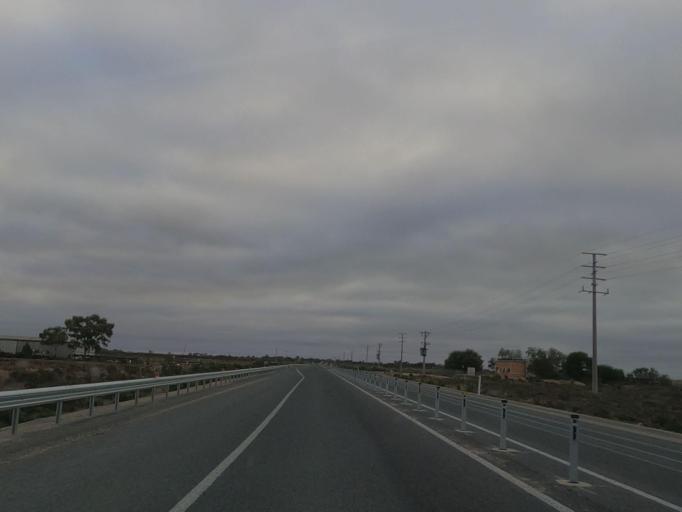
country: AU
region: Victoria
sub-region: Swan Hill
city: Swan Hill
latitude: -35.4759
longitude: 143.6801
